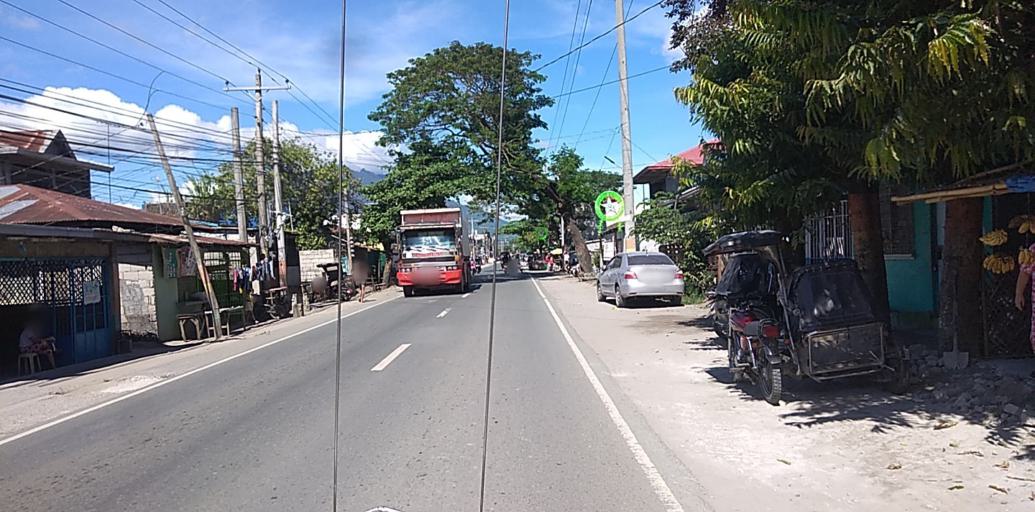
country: PH
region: Central Luzon
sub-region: Province of Pampanga
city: Arayat
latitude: 15.1281
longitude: 120.7755
